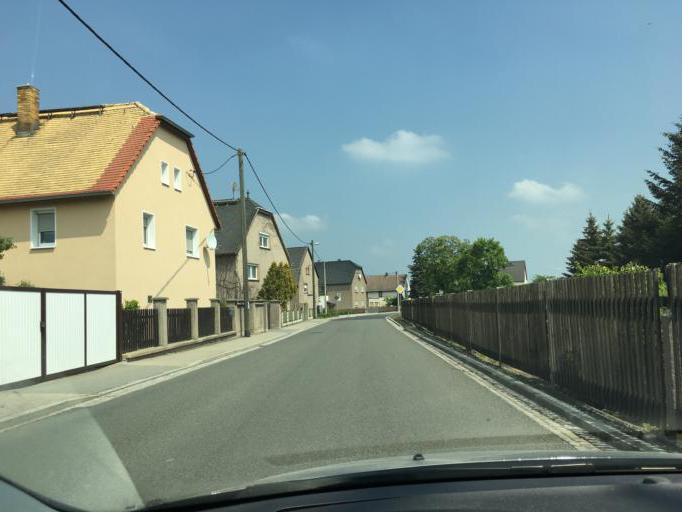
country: DE
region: Saxony
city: Grossbardau
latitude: 51.1846
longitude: 12.6642
